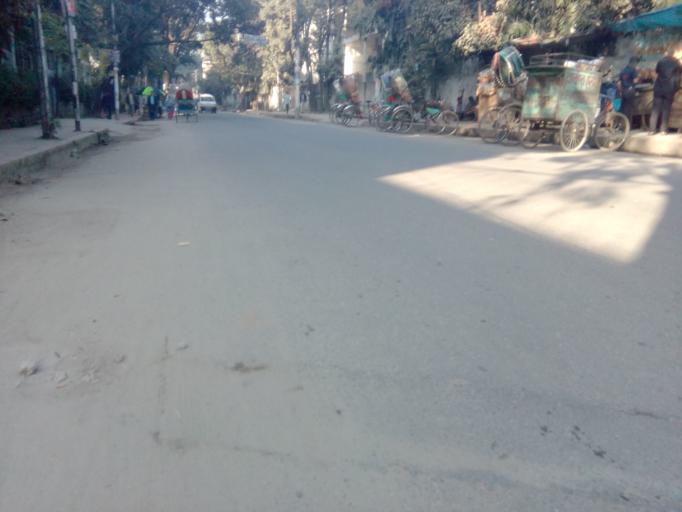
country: BD
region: Dhaka
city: Azimpur
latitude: 23.7440
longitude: 90.3838
